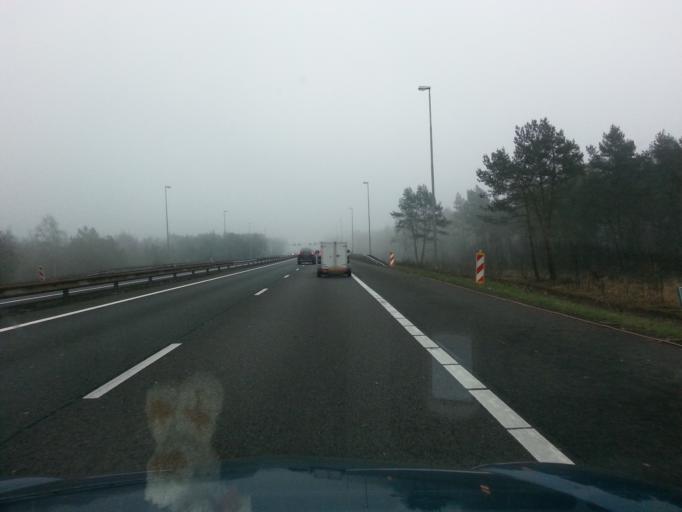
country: NL
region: Gelderland
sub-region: Gemeente Renkum
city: Heelsum
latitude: 52.0217
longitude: 5.7424
